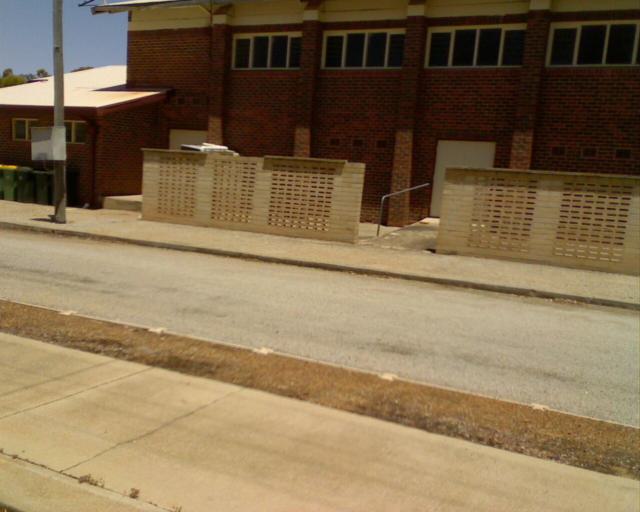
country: AU
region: Western Australia
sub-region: Wongan-Ballidu
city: Wongan Hills
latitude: -30.8272
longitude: 117.4822
